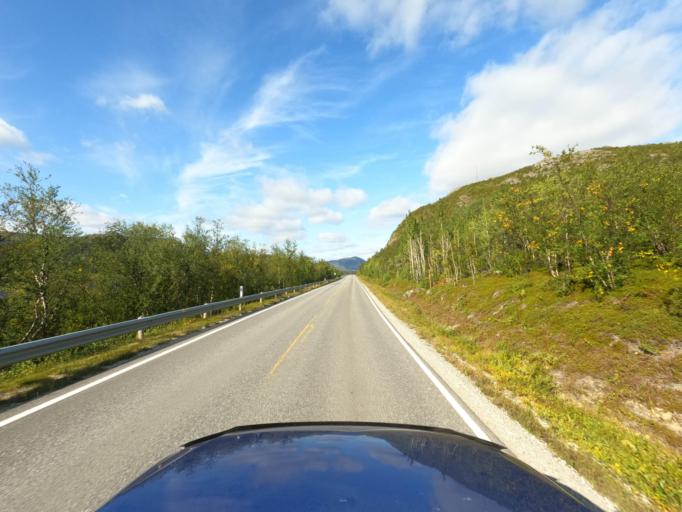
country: NO
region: Finnmark Fylke
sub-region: Porsanger
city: Lakselv
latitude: 69.9127
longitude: 24.9867
